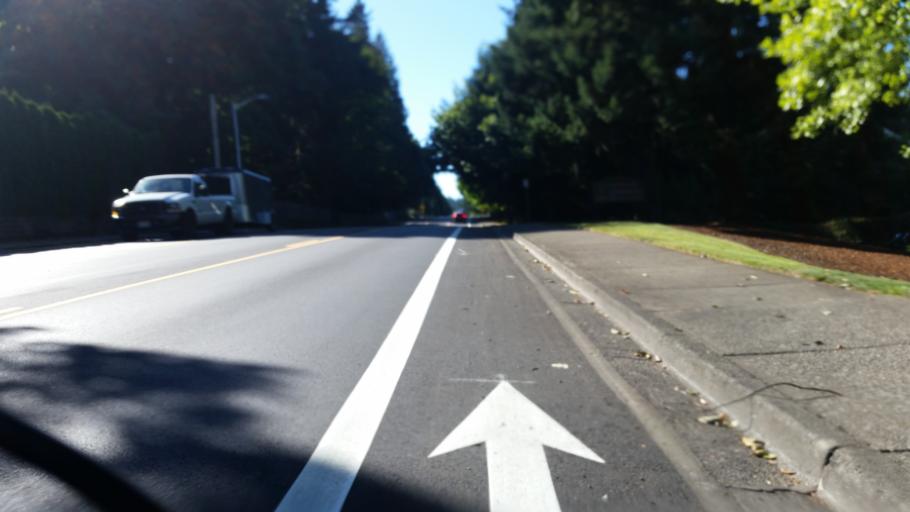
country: US
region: Oregon
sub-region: Washington County
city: Durham
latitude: 45.4152
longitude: -122.7559
